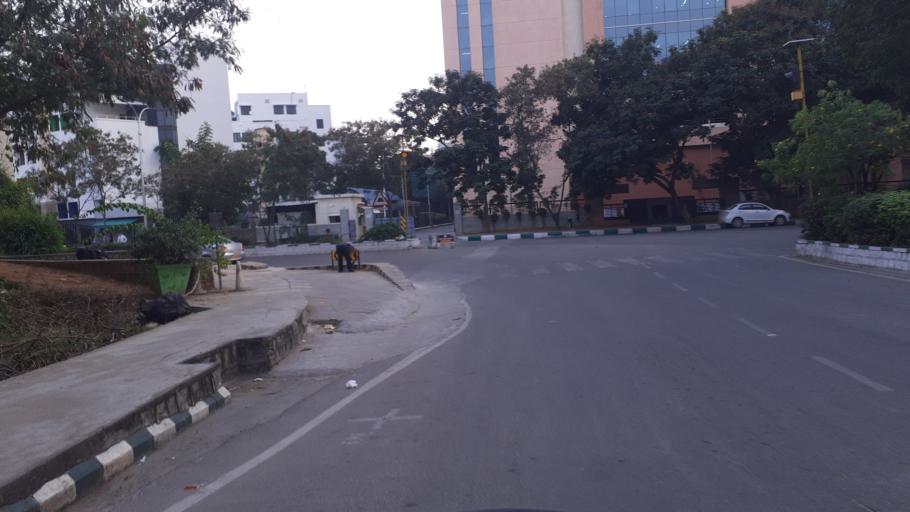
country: IN
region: Telangana
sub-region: Rangareddi
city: Kukatpalli
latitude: 17.4443
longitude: 78.3748
